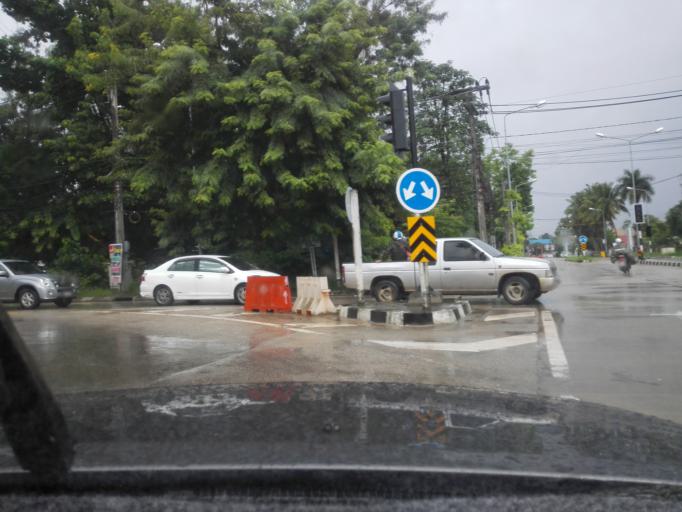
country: TH
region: Tak
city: Mae Sot
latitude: 16.7124
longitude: 98.5748
